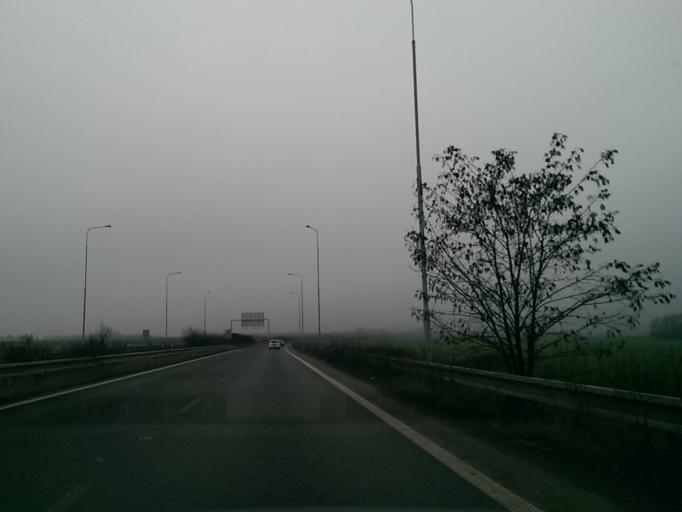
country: CZ
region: Olomoucky
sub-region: Okres Olomouc
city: Olomouc
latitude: 49.6039
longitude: 17.2175
